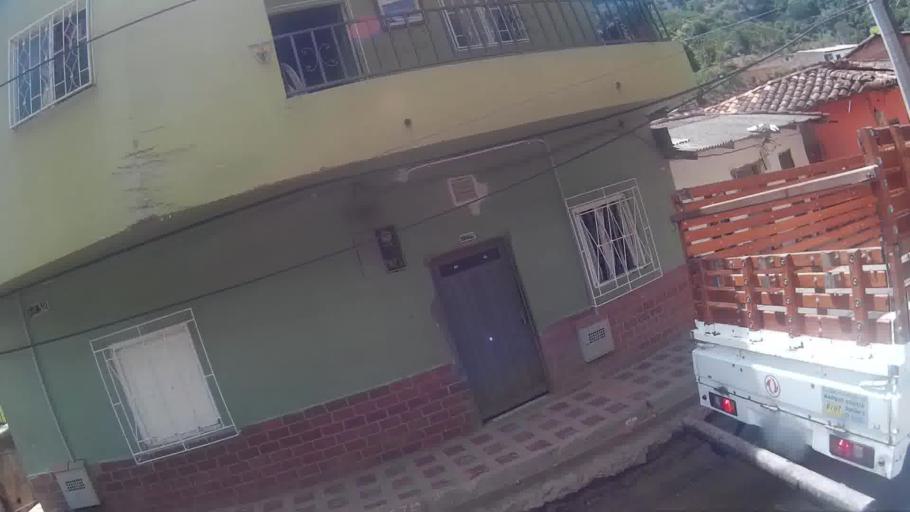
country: CO
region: Antioquia
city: Salgar
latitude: 5.9647
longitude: -75.9819
